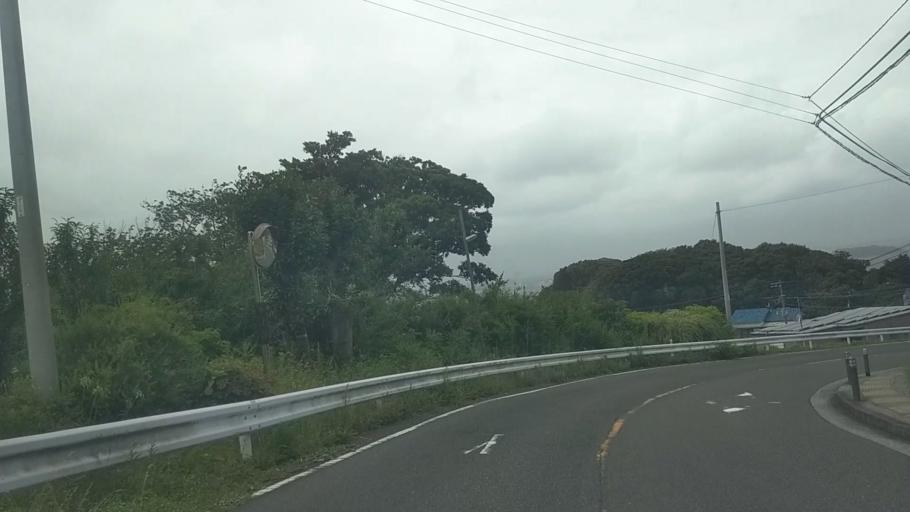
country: JP
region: Kanagawa
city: Yokosuka
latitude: 35.2553
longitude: 139.7192
